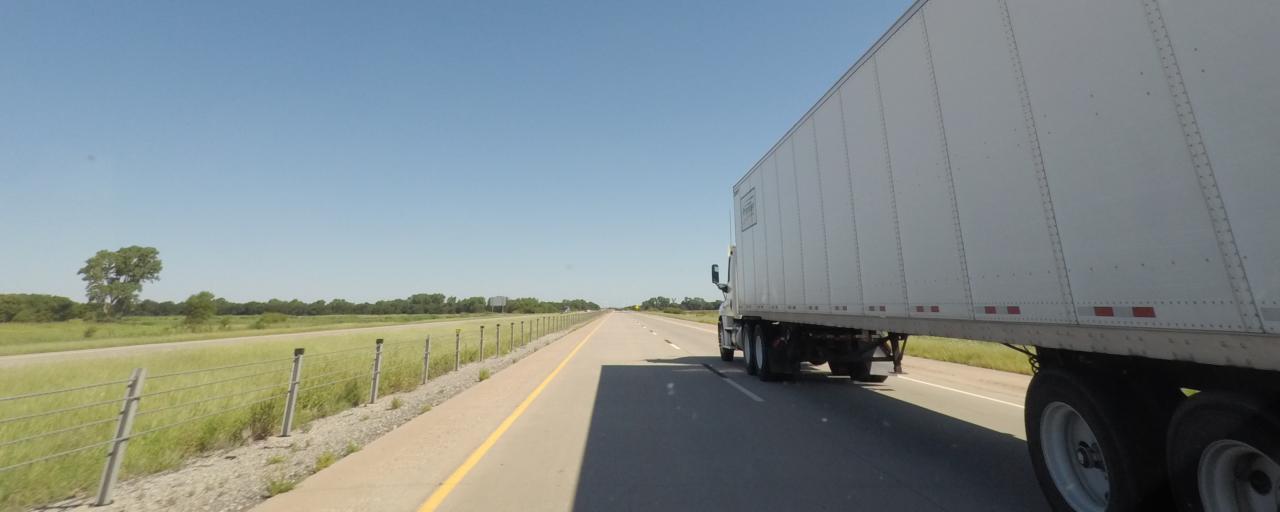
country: US
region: Oklahoma
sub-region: Noble County
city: Perry
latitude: 36.4645
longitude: -97.3272
